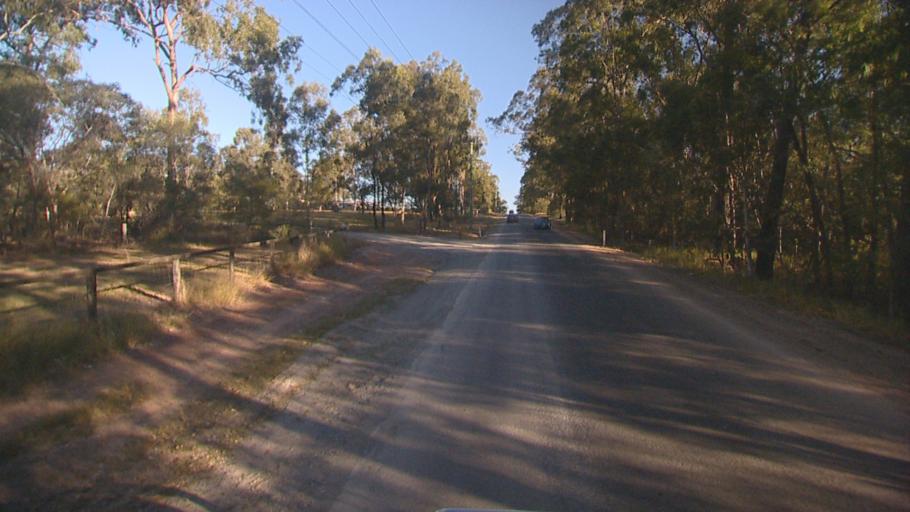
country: AU
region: Queensland
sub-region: Logan
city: Chambers Flat
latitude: -27.7758
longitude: 153.1365
